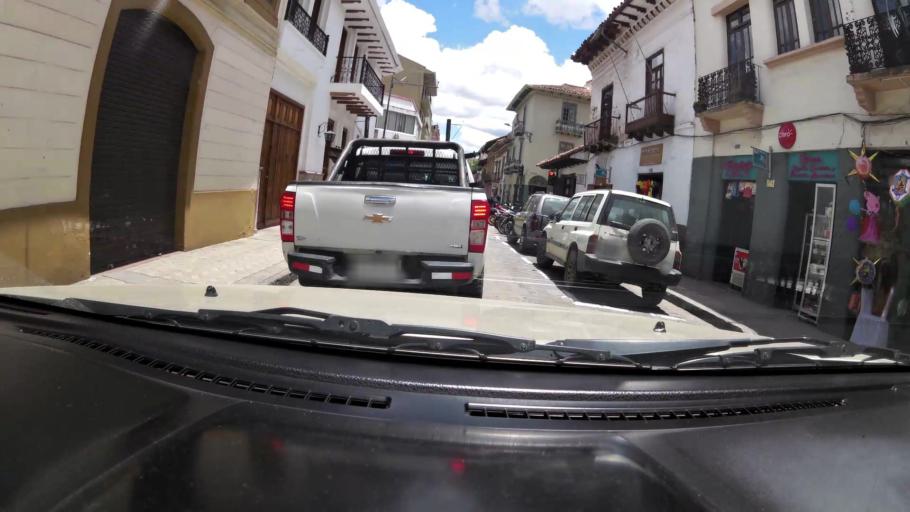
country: EC
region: Azuay
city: Cuenca
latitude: -2.8972
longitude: -79.0073
